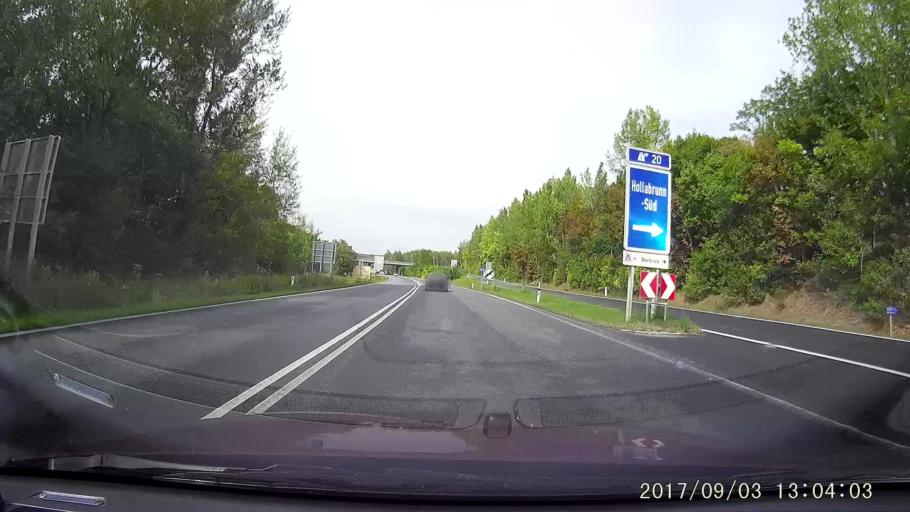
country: AT
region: Lower Austria
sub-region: Politischer Bezirk Hollabrunn
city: Hollabrunn
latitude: 48.5447
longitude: 16.0793
